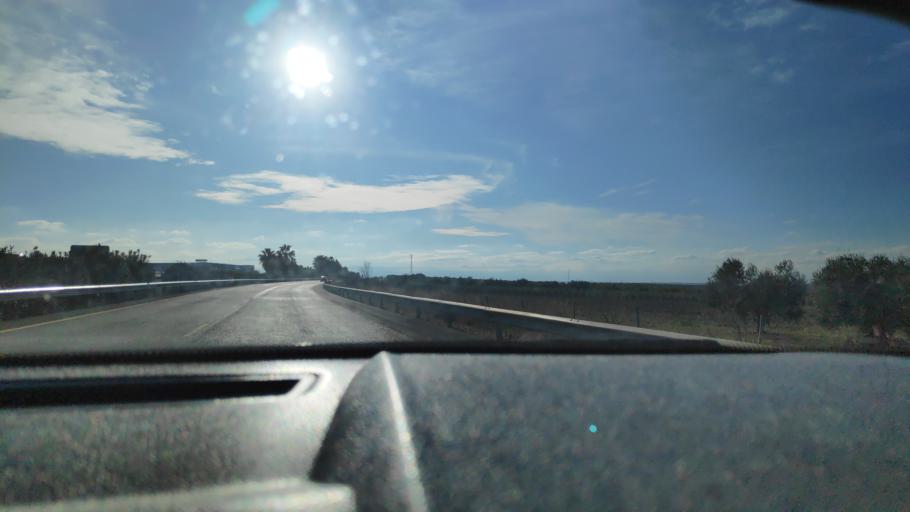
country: ES
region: Andalusia
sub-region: Provincia de Sevilla
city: Ecija
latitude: 37.5811
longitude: -4.9935
